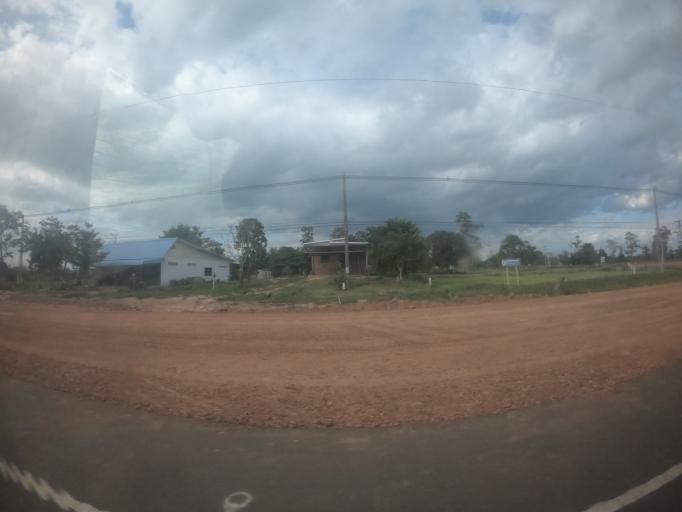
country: TH
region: Surin
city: Kap Choeng
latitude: 14.5145
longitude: 103.5485
